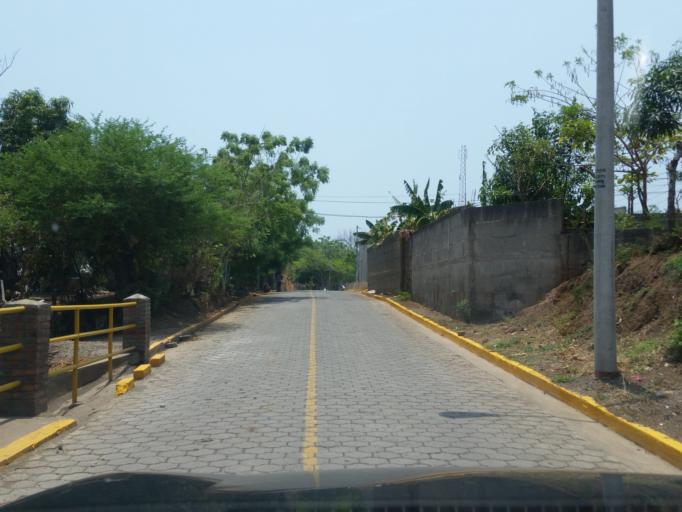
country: NI
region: Granada
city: Granada
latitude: 11.9317
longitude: -85.9717
